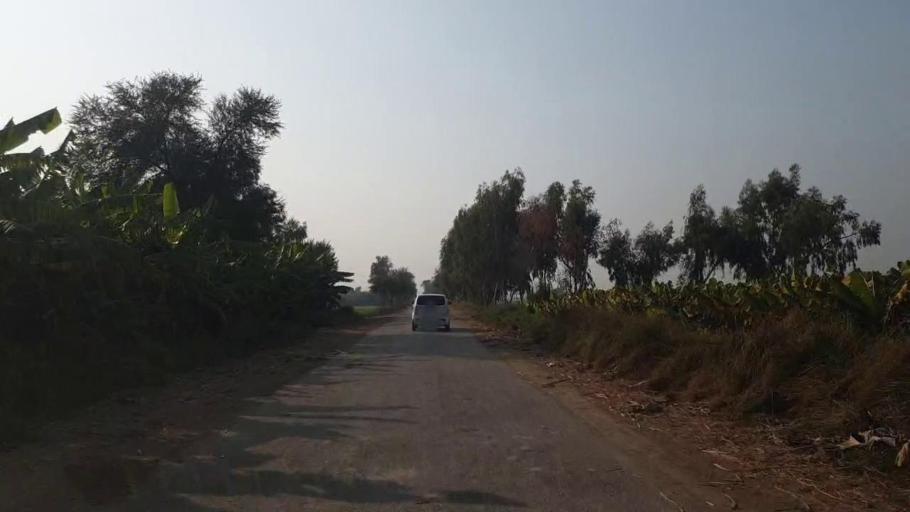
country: PK
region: Sindh
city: Shahdadpur
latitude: 25.9713
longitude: 68.5359
